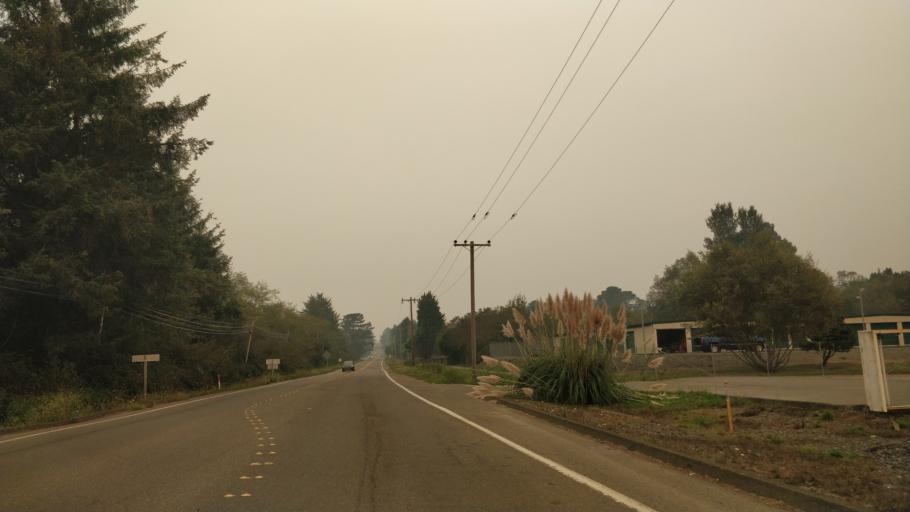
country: US
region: California
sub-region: Humboldt County
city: McKinleyville
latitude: 40.9563
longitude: -124.1008
